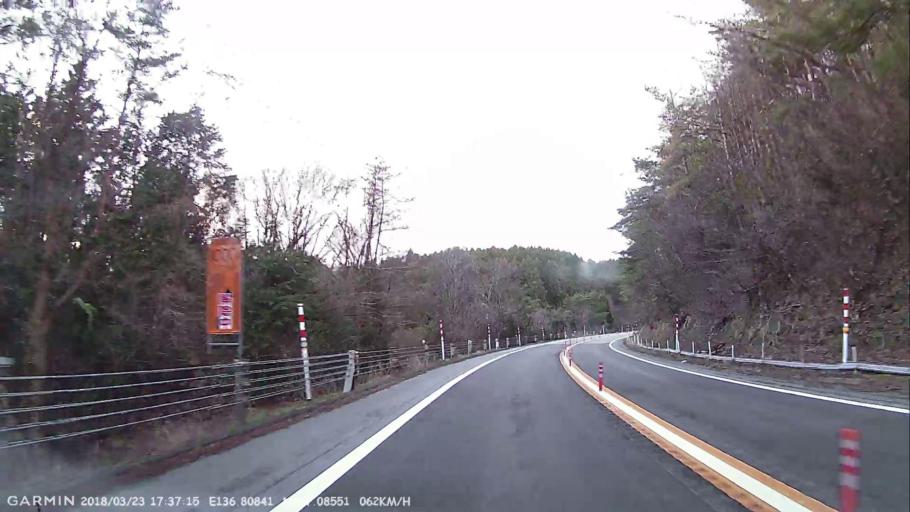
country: JP
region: Ishikawa
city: Nanao
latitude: 37.0856
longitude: 136.8083
